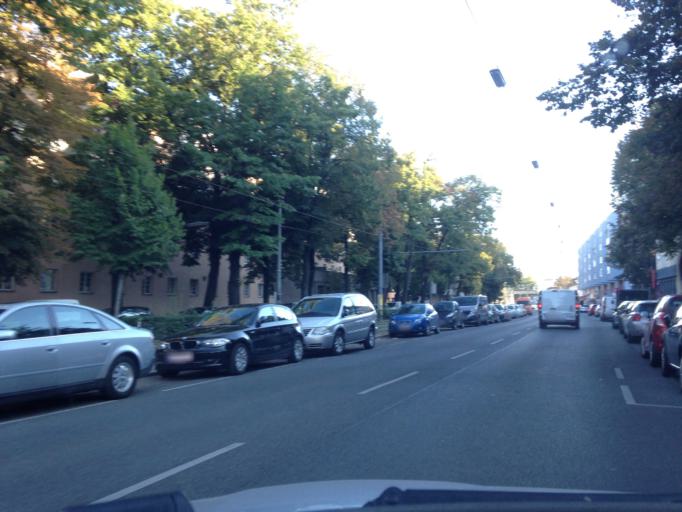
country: AT
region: Vienna
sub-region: Wien Stadt
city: Vienna
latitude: 48.2466
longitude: 16.3618
